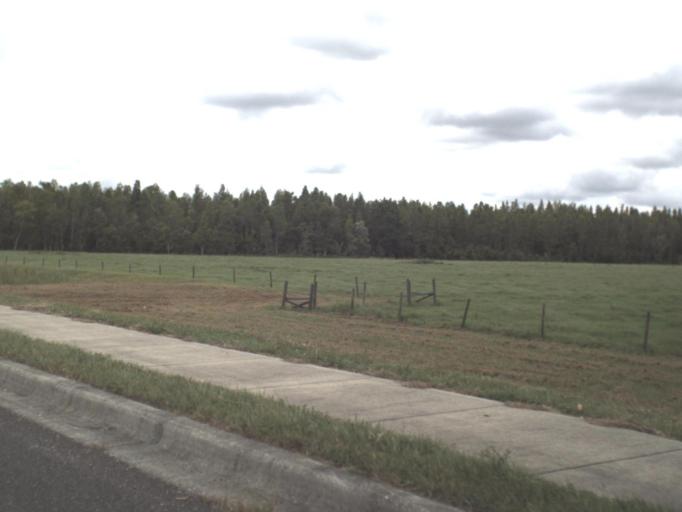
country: US
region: Florida
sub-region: Pasco County
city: Trinity
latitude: 28.1951
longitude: -82.6414
